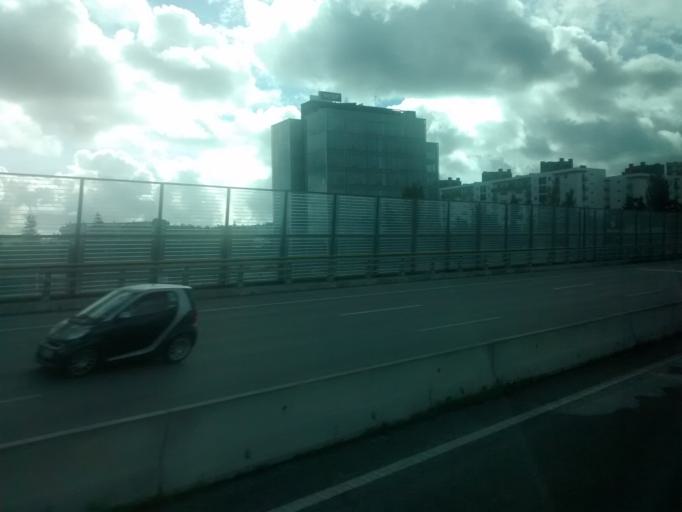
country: PT
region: Lisbon
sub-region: Odivelas
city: Olival do Basto
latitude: 38.7718
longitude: -9.1647
